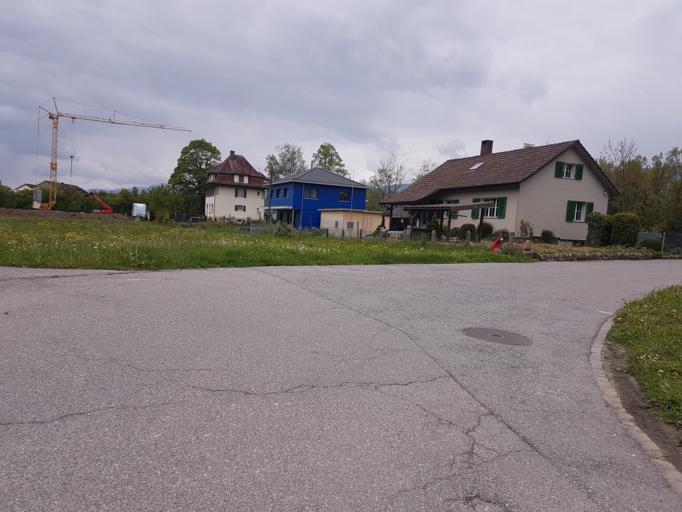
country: CH
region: Bern
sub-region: Oberaargau
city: Wangen an der Aare
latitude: 47.2344
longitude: 7.6647
